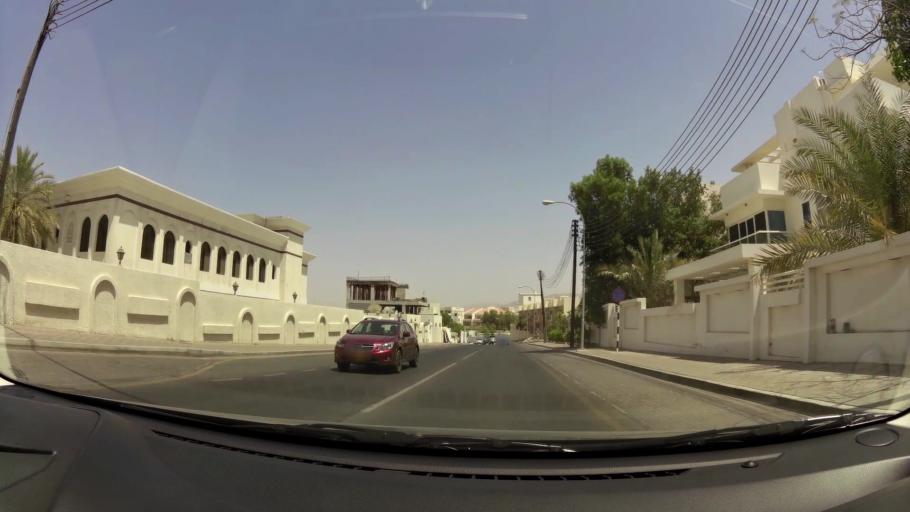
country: OM
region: Muhafazat Masqat
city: Muscat
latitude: 23.6246
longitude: 58.4861
